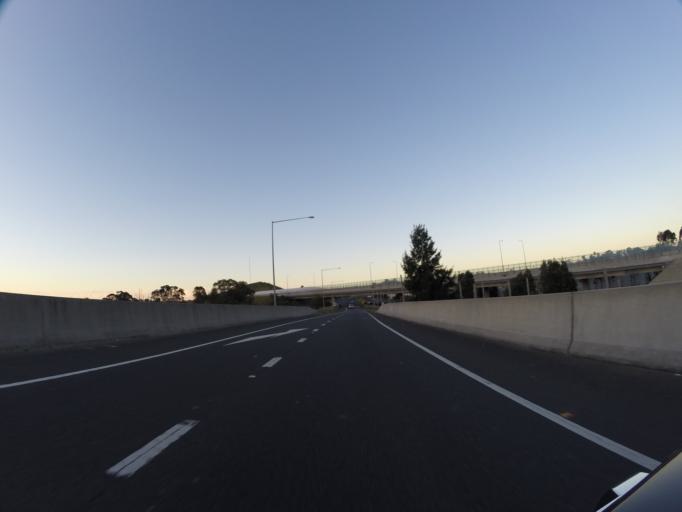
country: AU
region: New South Wales
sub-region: Campbelltown Municipality
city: Glenfield
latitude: -33.9534
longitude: 150.8771
